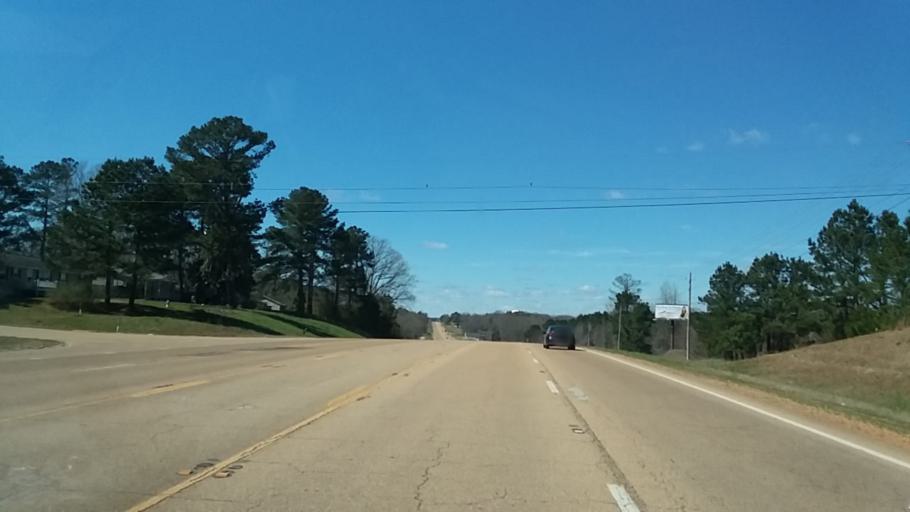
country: US
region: Mississippi
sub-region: Alcorn County
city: Farmington
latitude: 34.8968
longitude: -88.4708
